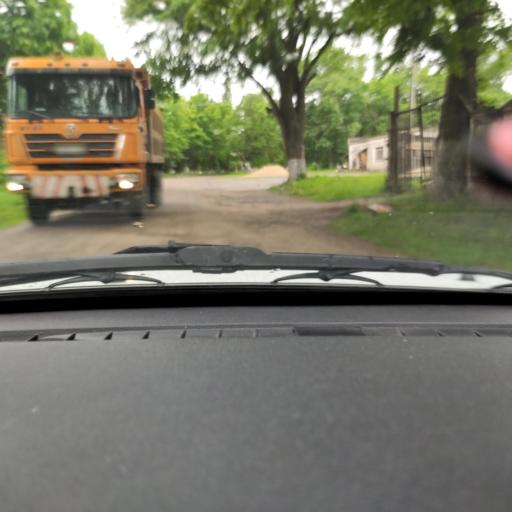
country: RU
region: Voronezj
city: Devitsa
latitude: 51.6062
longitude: 39.0012
